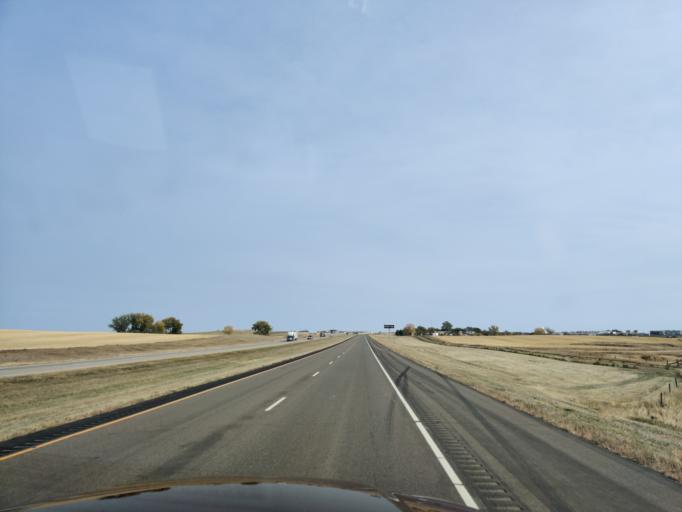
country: US
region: North Dakota
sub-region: Stark County
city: Dickinson
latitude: 46.8931
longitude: -102.7572
